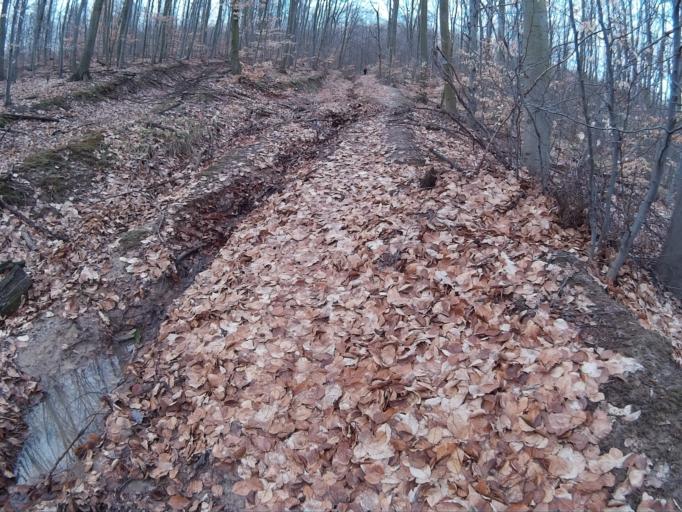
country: HU
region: Borsod-Abauj-Zemplen
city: Tolcsva
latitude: 48.3552
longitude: 21.4935
